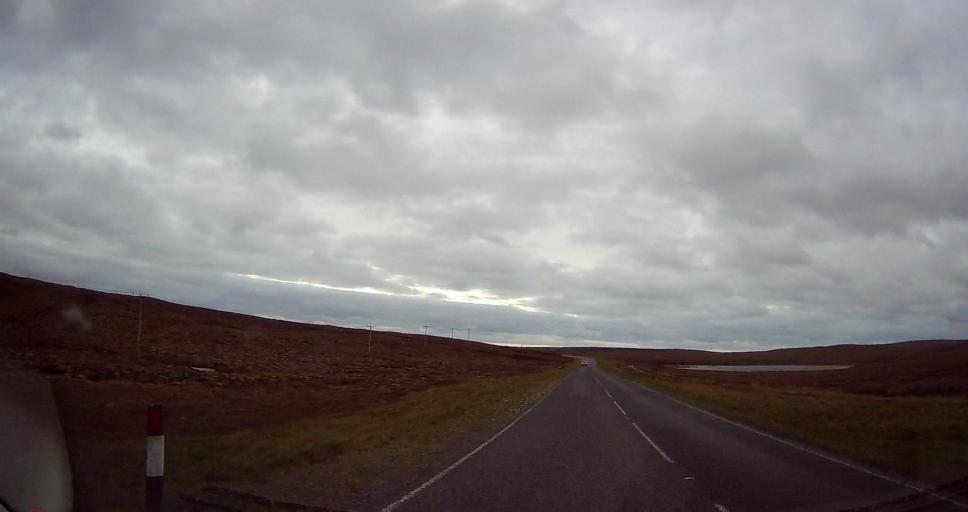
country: GB
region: Scotland
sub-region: Shetland Islands
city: Shetland
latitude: 60.6646
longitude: -1.0248
